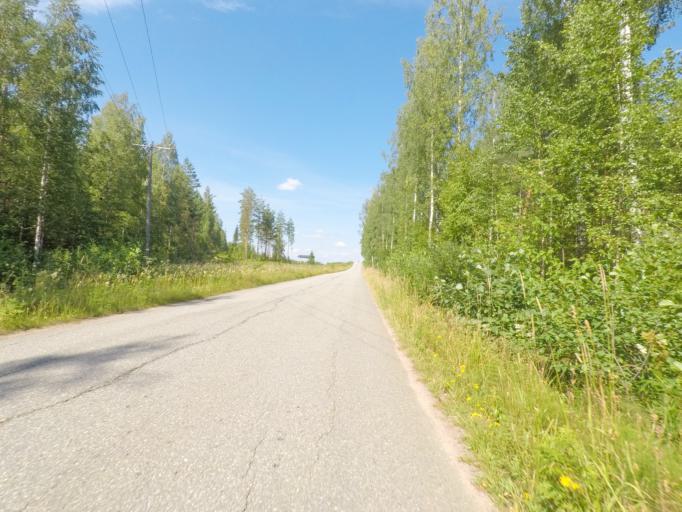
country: FI
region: Southern Savonia
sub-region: Mikkeli
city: Puumala
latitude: 61.4117
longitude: 28.0925
